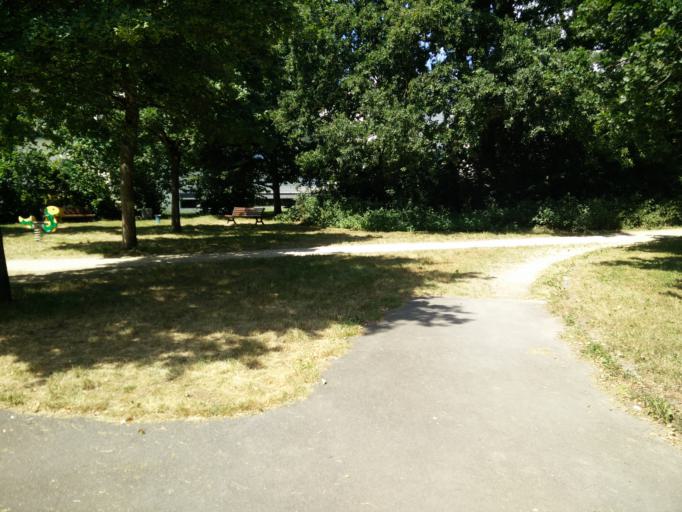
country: FR
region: Brittany
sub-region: Departement d'Ille-et-Vilaine
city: Saint-Gregoire
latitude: 48.1375
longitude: -1.6706
